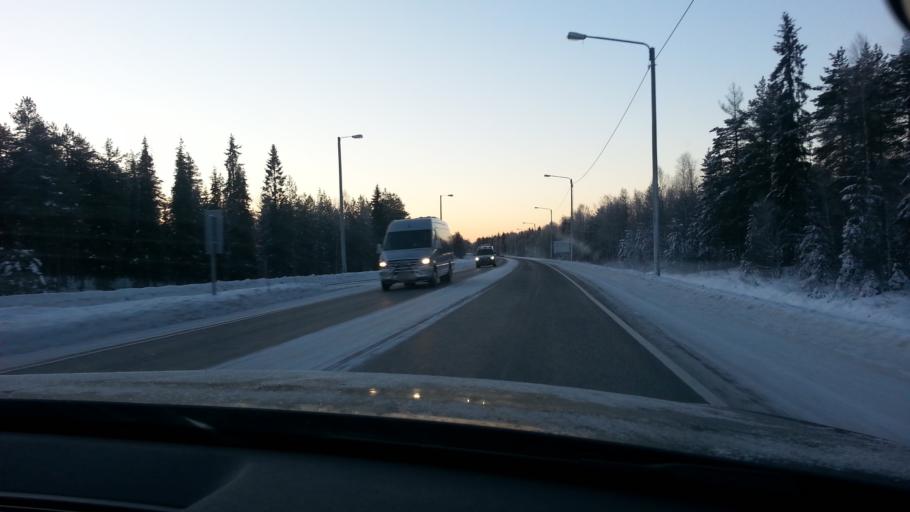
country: FI
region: Lapland
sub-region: Rovaniemi
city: Rovaniemi
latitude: 66.5303
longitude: 25.7646
